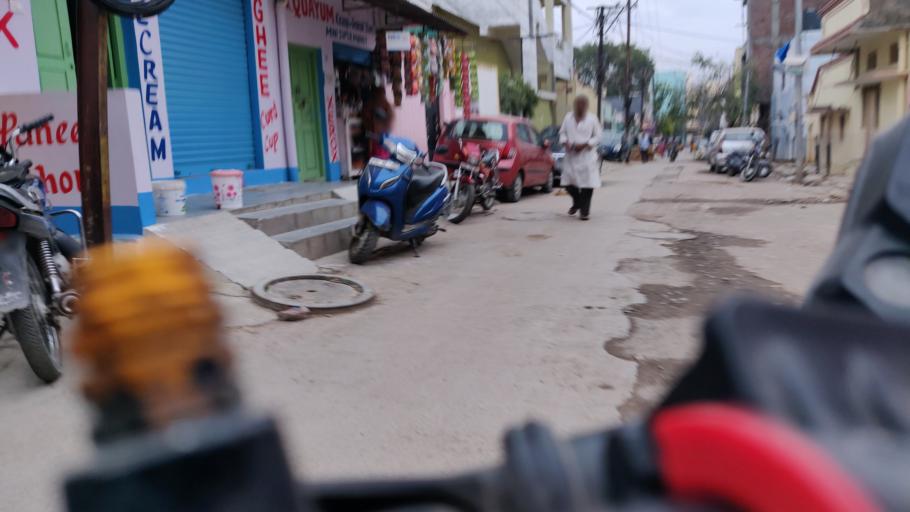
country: IN
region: Telangana
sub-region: Rangareddi
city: Kukatpalli
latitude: 17.4523
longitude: 78.4115
